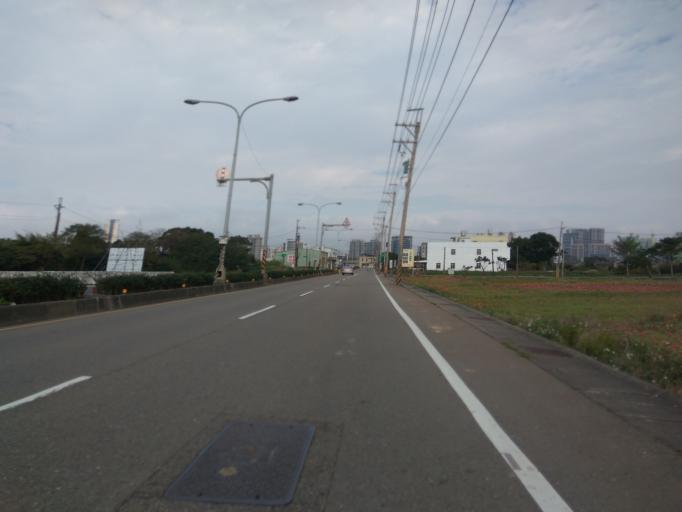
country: TW
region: Taiwan
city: Taoyuan City
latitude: 24.9965
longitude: 121.2195
